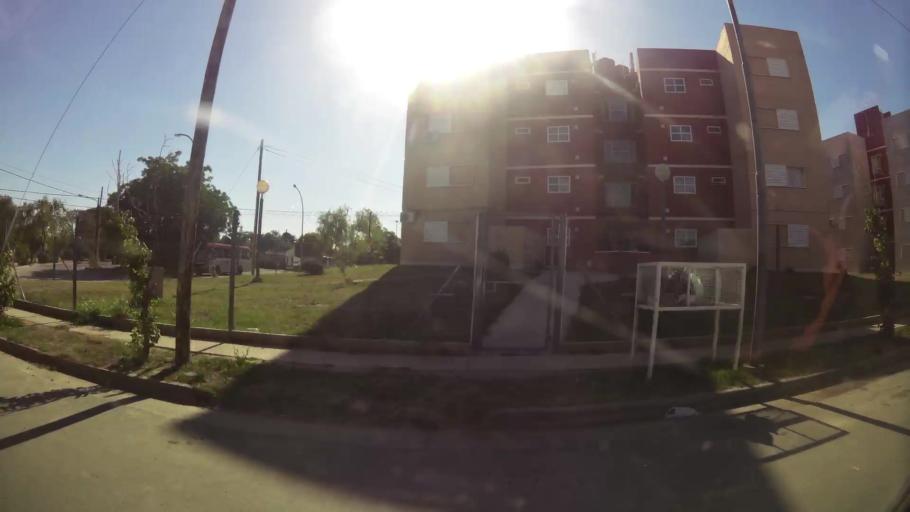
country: AR
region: Cordoba
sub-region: Departamento de Capital
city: Cordoba
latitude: -31.3572
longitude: -64.1889
